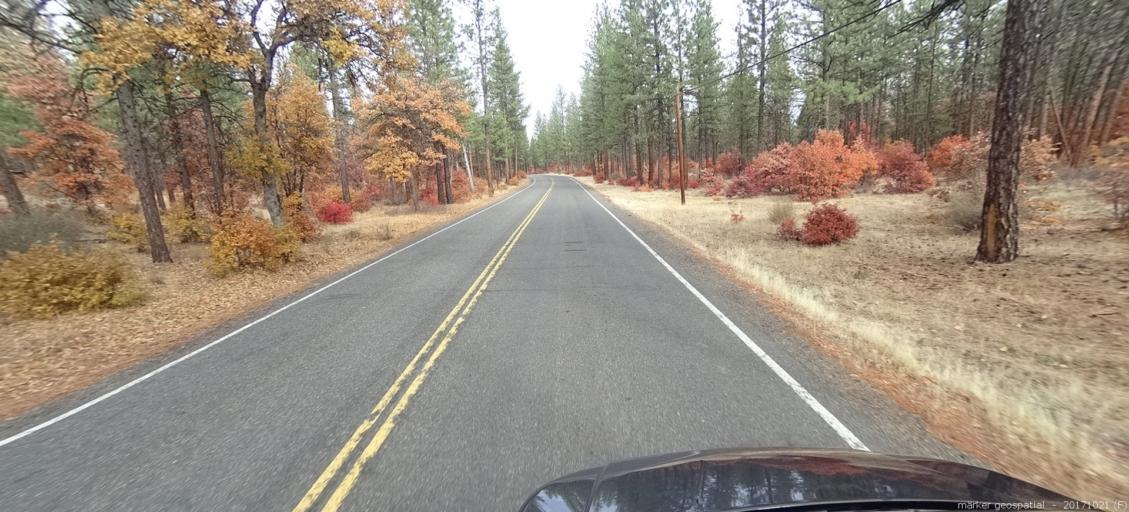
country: US
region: California
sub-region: Shasta County
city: Burney
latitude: 40.9542
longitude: -121.5749
